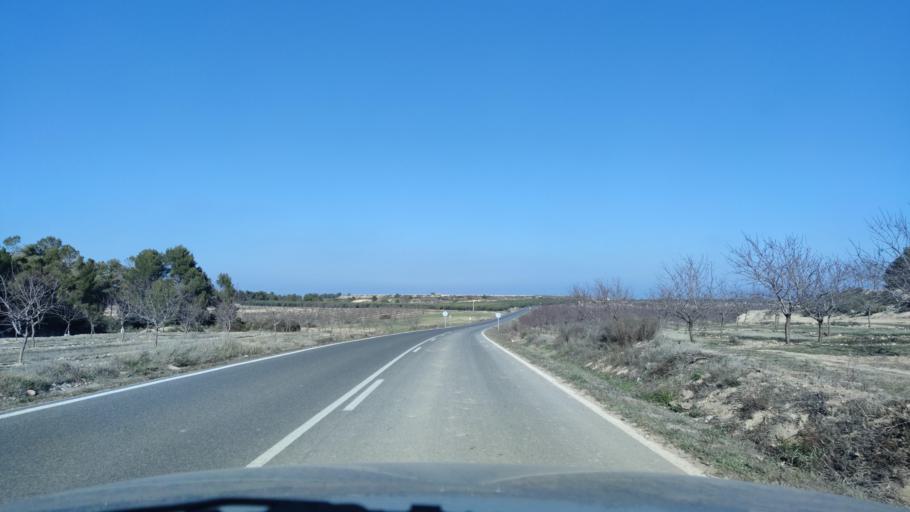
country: ES
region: Catalonia
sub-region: Provincia de Lleida
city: Maials
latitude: 41.3497
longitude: 0.4694
